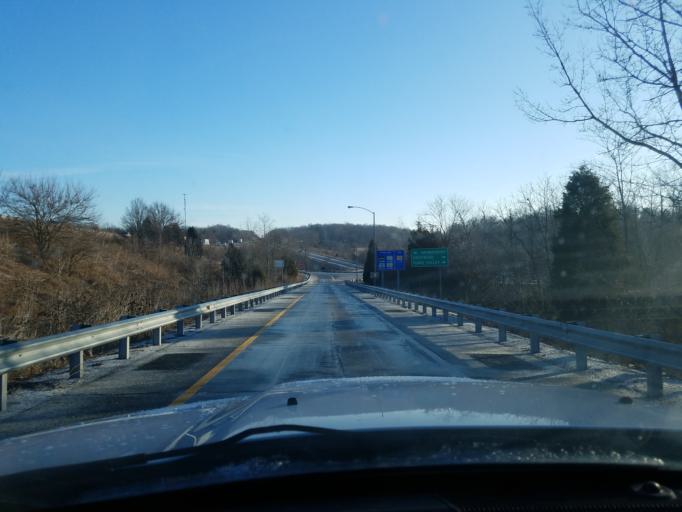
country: US
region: Kentucky
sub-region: Oldham County
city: Crestwood
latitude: 38.3454
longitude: -85.4928
